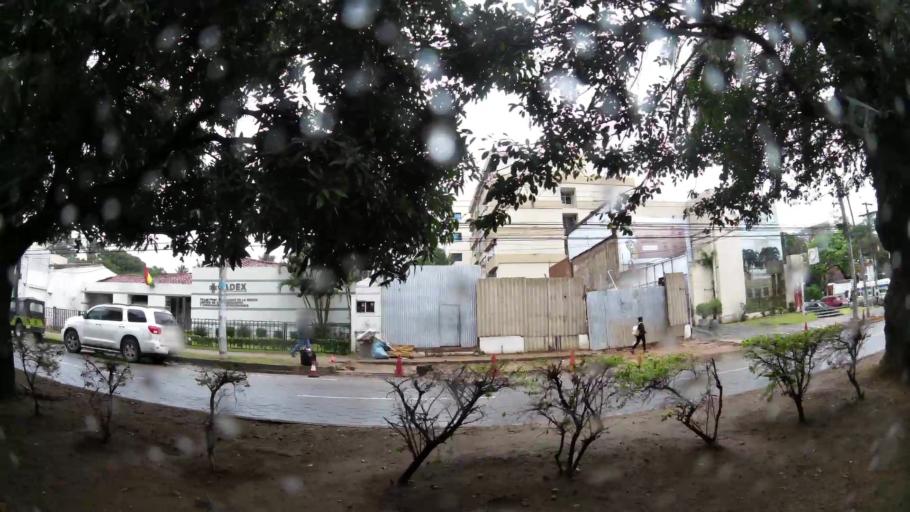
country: BO
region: Santa Cruz
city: Santa Cruz de la Sierra
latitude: -17.7929
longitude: -63.1813
